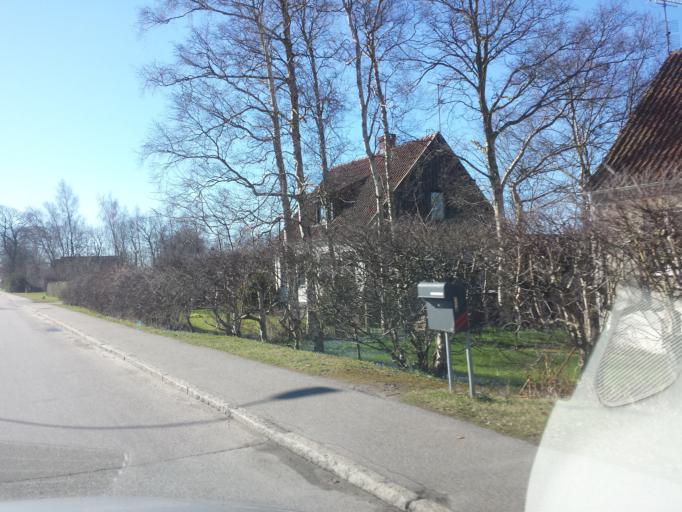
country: SE
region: Skane
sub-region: Sjobo Kommun
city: Sjoebo
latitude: 55.6412
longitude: 13.7051
